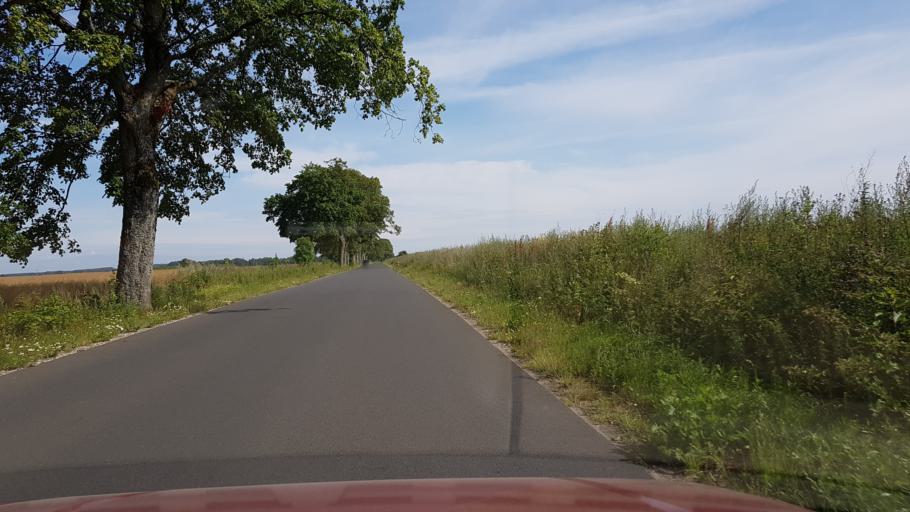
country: PL
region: West Pomeranian Voivodeship
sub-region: Powiat koszalinski
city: Polanow
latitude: 54.1389
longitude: 16.6209
